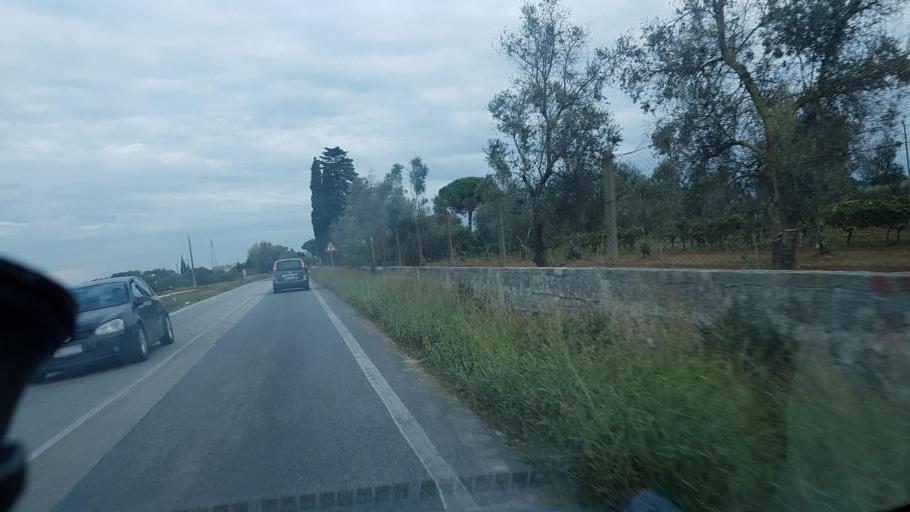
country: IT
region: Apulia
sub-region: Provincia di Brindisi
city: Oria
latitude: 40.5139
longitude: 17.6168
